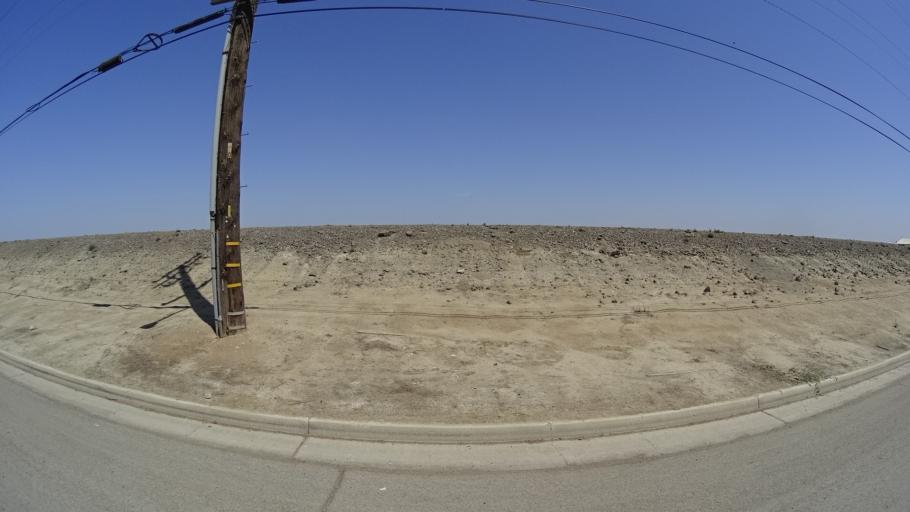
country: US
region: California
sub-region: Kings County
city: Home Garden
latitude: 36.2840
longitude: -119.6474
